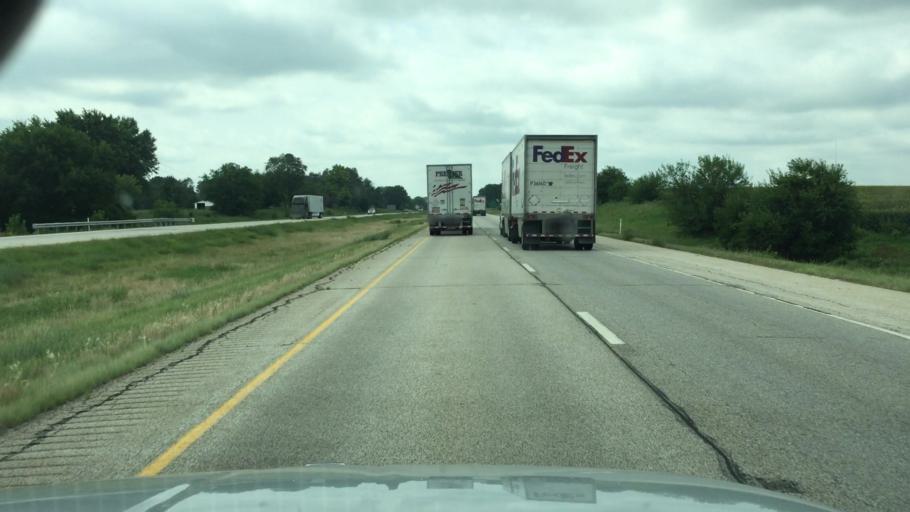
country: US
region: Illinois
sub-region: Knox County
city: Galesburg
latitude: 40.9603
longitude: -90.3318
